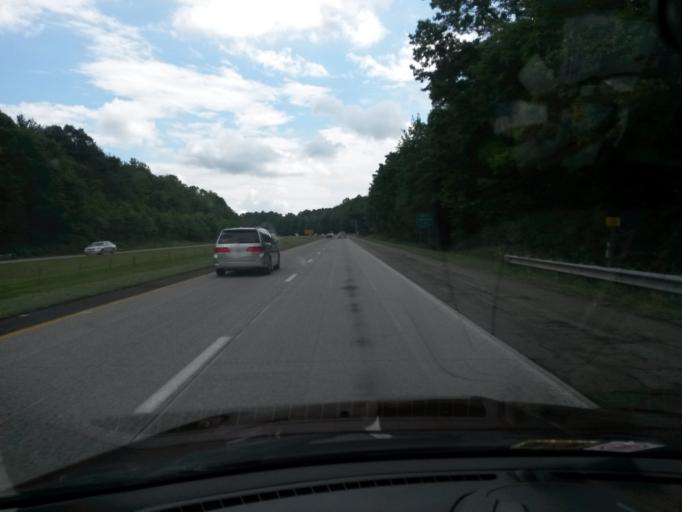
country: US
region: Virginia
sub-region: Carroll County
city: Cana
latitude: 36.5414
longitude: -80.7491
